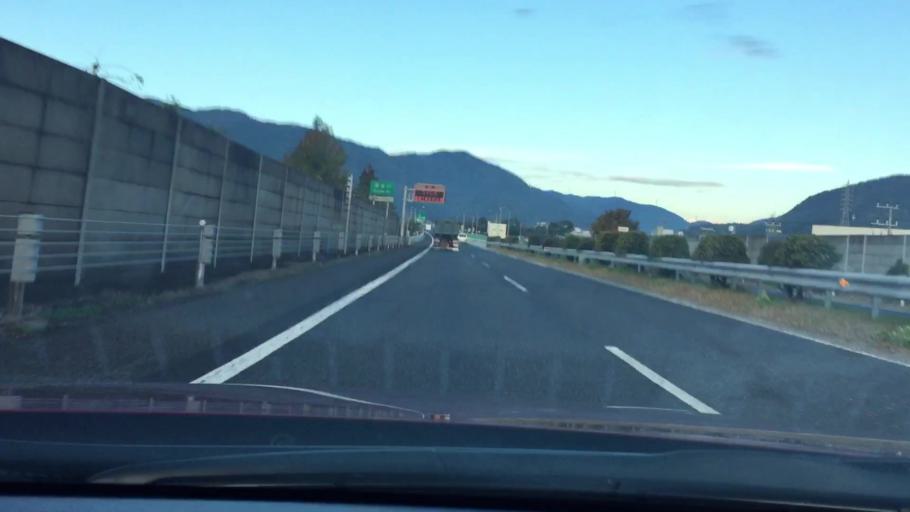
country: JP
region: Hyogo
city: Yamazakicho-nakabirose
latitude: 34.9978
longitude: 134.5554
